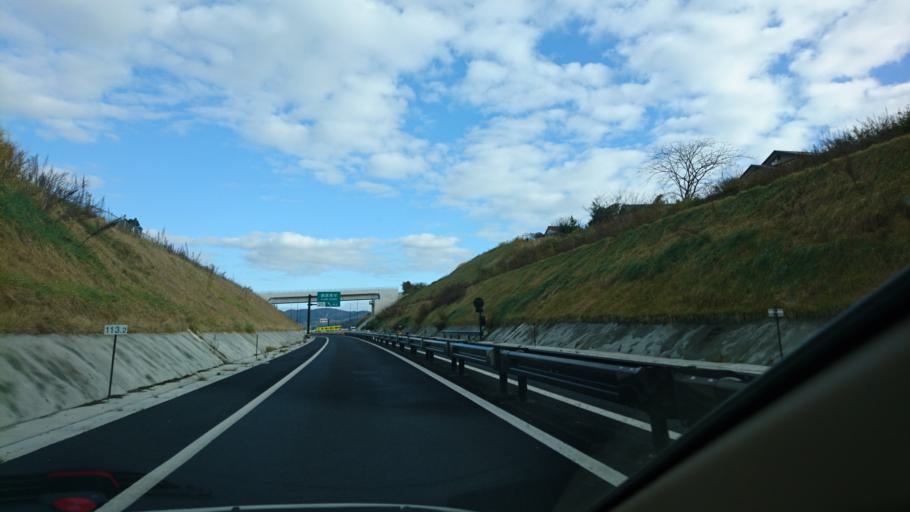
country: JP
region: Iwate
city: Ofunato
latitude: 38.8789
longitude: 141.5850
